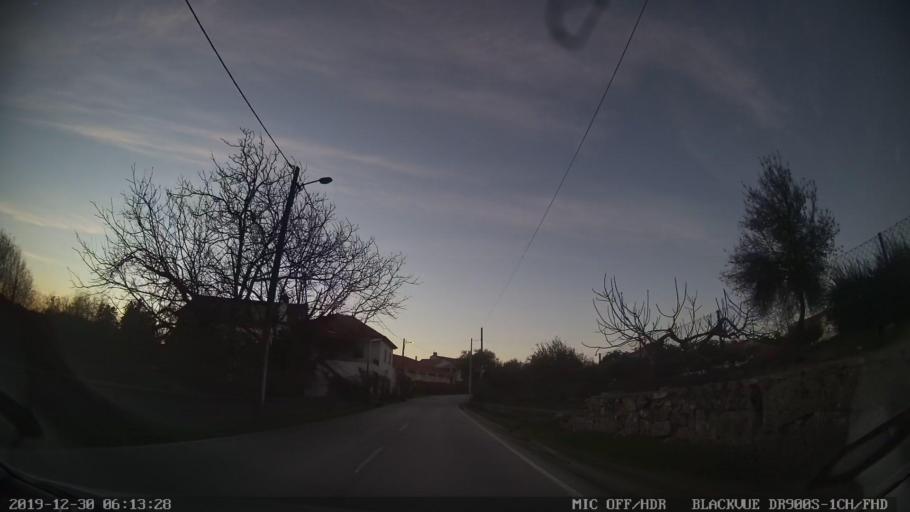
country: PT
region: Castelo Branco
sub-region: Penamacor
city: Penamacor
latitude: 40.1117
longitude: -7.2106
